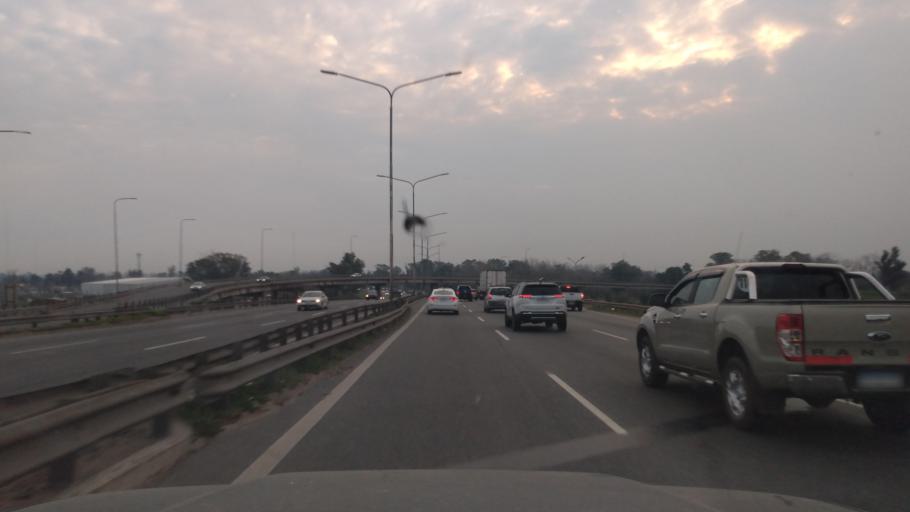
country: AR
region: Buenos Aires
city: Hurlingham
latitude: -34.5687
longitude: -58.6519
